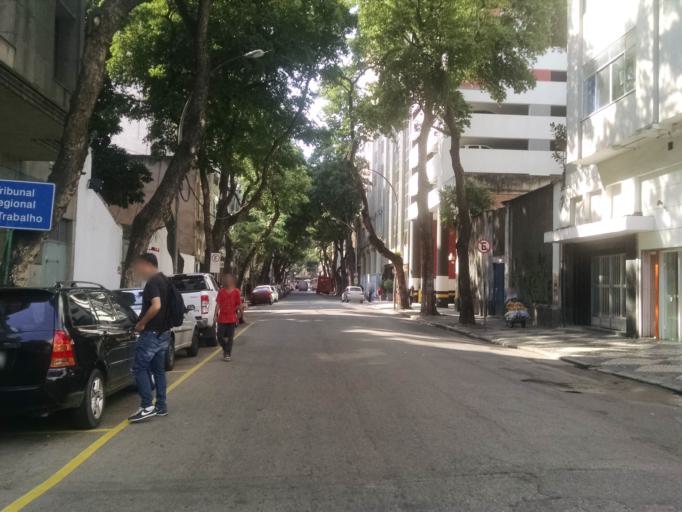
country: BR
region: Rio de Janeiro
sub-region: Rio De Janeiro
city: Rio de Janeiro
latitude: -22.9108
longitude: -43.1839
